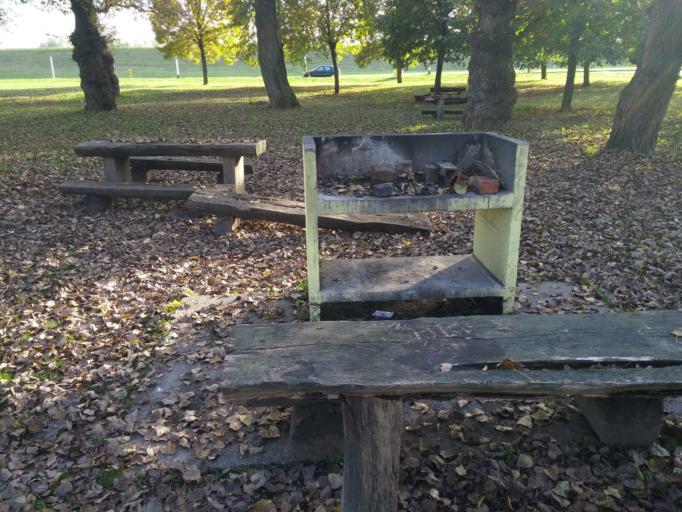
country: HR
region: Grad Zagreb
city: Jankomir
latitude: 45.7794
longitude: 15.9107
